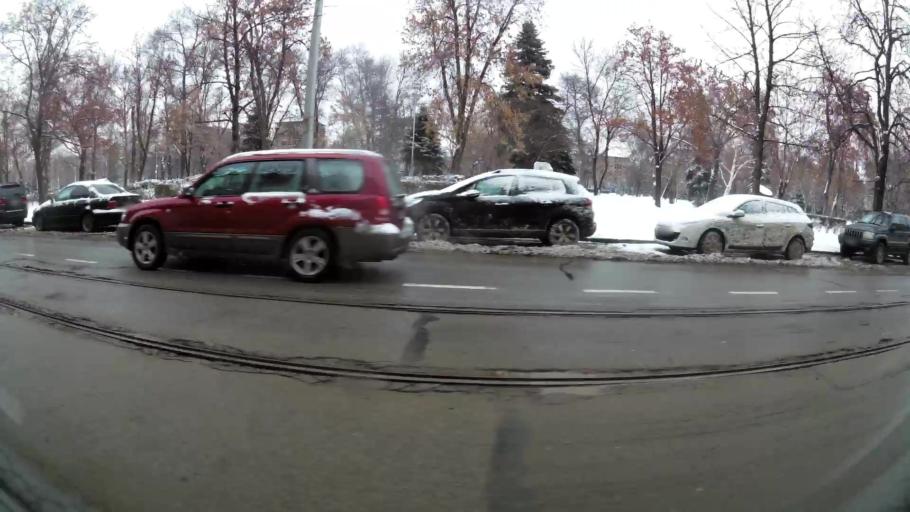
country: BG
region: Sofia-Capital
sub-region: Stolichna Obshtina
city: Sofia
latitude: 42.6964
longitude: 23.3435
